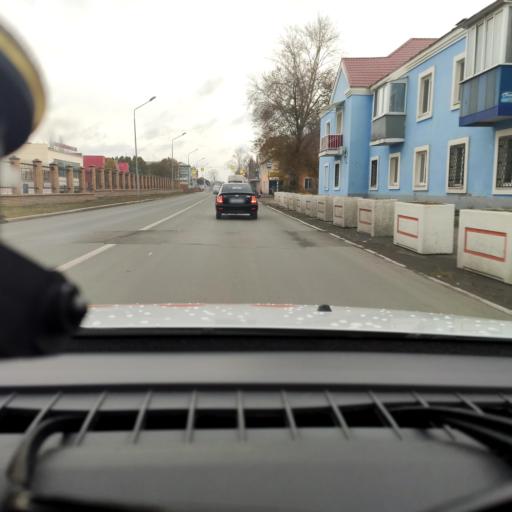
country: RU
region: Samara
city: Chapayevsk
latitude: 52.9848
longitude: 49.7134
